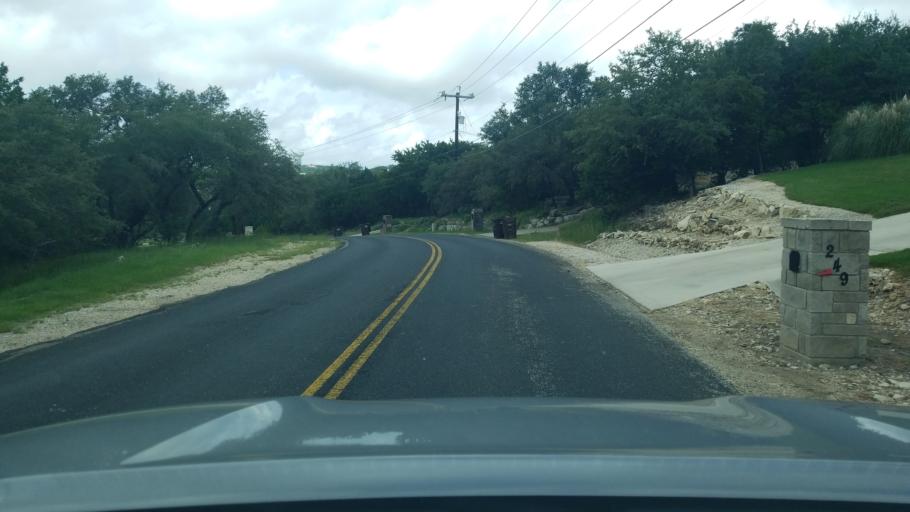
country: US
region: Texas
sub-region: Bexar County
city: Timberwood Park
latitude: 29.6846
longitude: -98.4923
